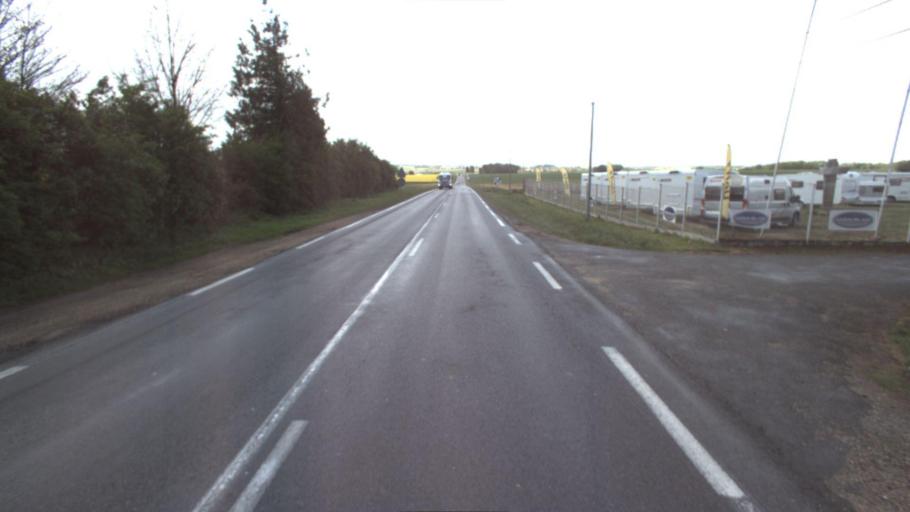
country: FR
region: Ile-de-France
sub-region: Departement de Seine-et-Marne
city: Jouy-le-Chatel
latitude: 48.6882
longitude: 3.1240
